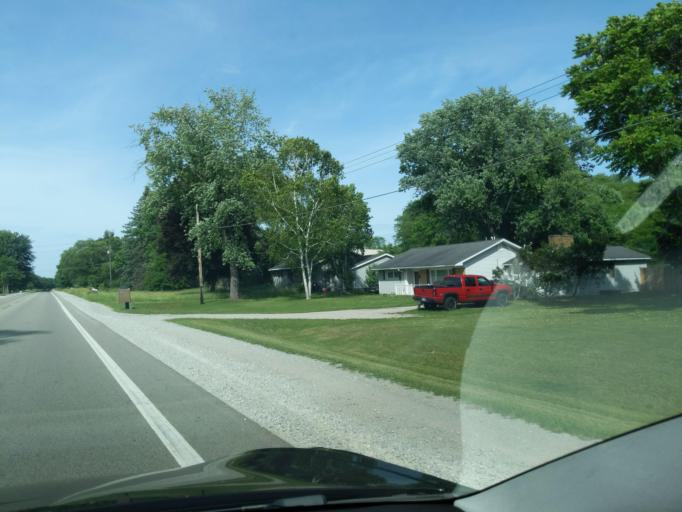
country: US
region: Michigan
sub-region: Muskegon County
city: Twin Lake
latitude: 43.4158
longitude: -86.0728
